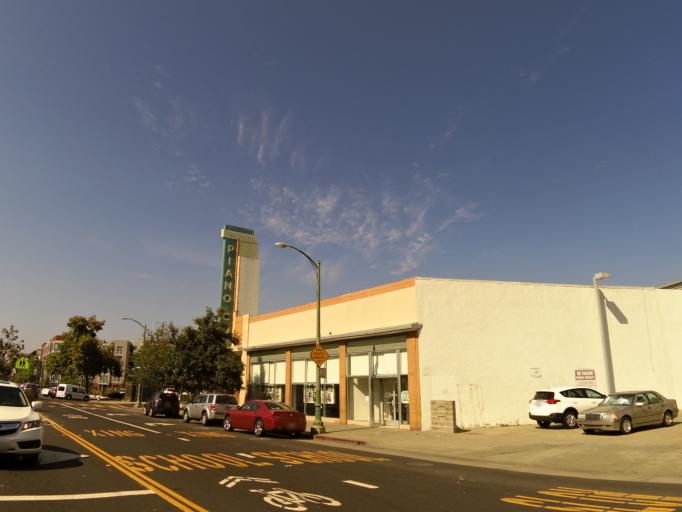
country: US
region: California
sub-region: Alameda County
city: Oakland
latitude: 37.8073
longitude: -122.2723
